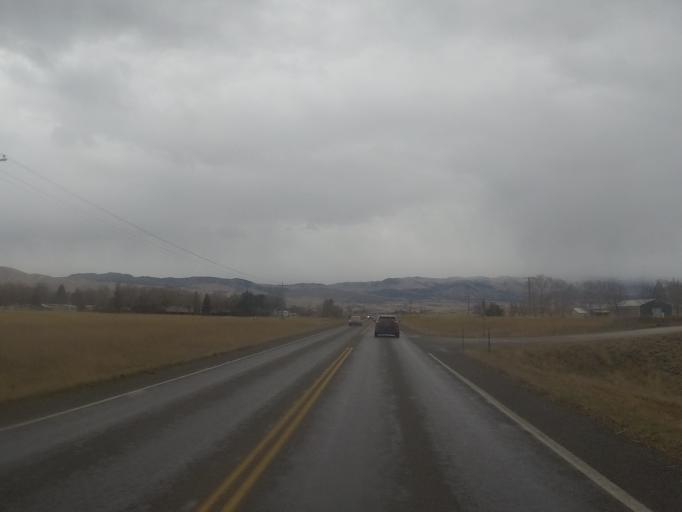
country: US
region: Montana
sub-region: Broadwater County
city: Townsend
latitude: 46.3220
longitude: -111.4780
